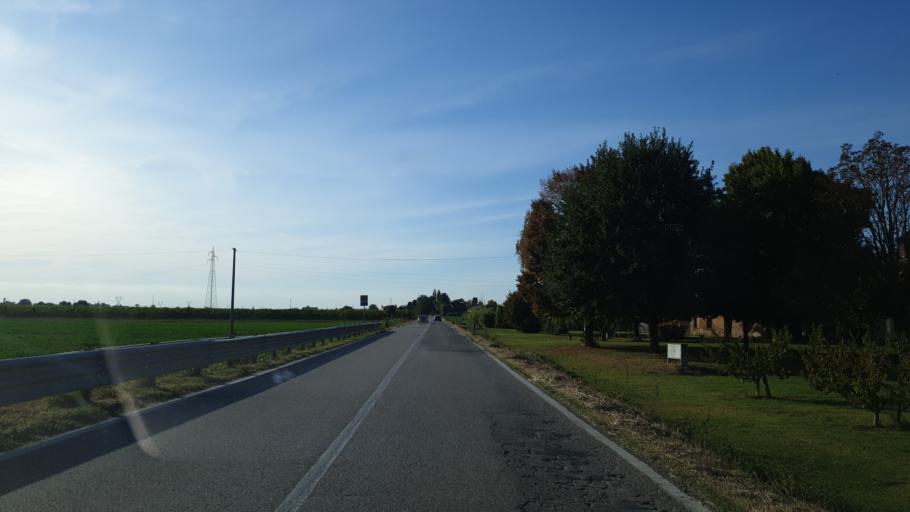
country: IT
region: Emilia-Romagna
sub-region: Provincia di Ravenna
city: Voltana
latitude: 44.5416
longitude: 11.9847
